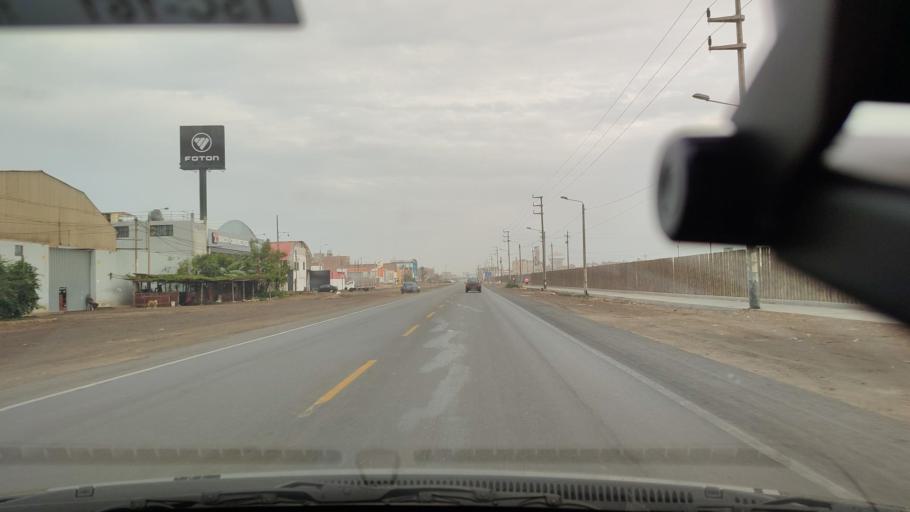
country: PE
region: La Libertad
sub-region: Provincia de Trujillo
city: Buenos Aires
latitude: -8.1477
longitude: -79.0443
